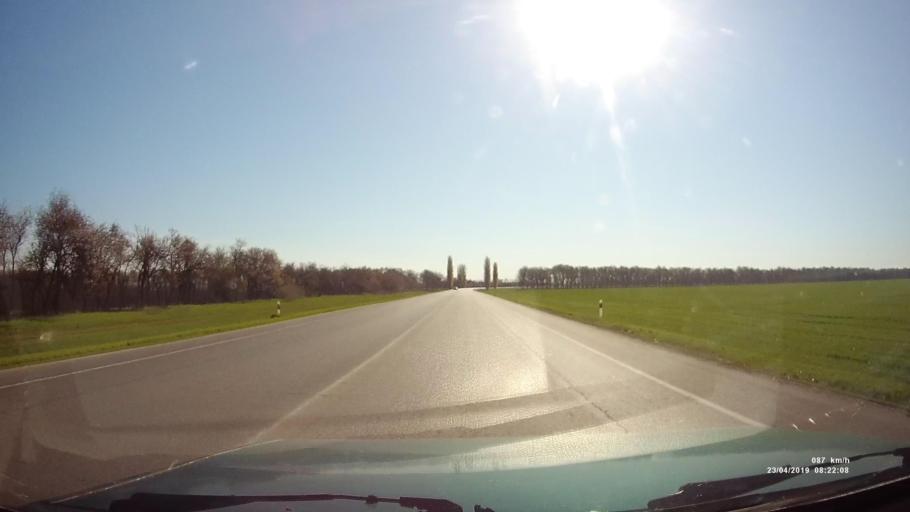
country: RU
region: Rostov
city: Tselina
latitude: 46.5363
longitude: 40.9042
